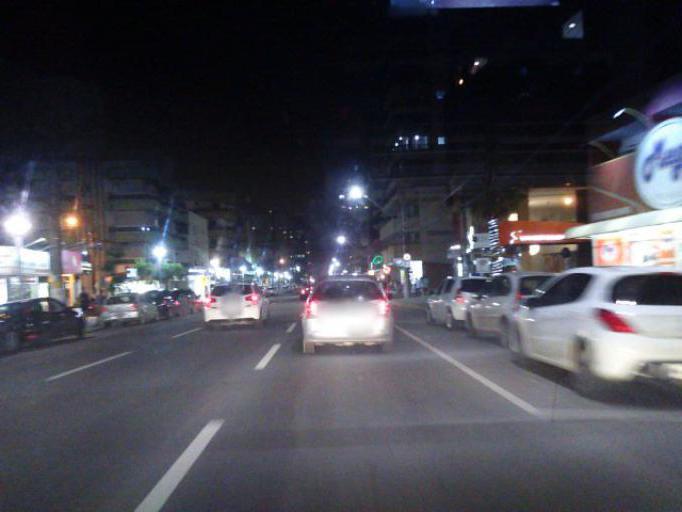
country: BR
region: Santa Catarina
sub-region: Itapema
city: Itapema
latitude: -27.1317
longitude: -48.5995
